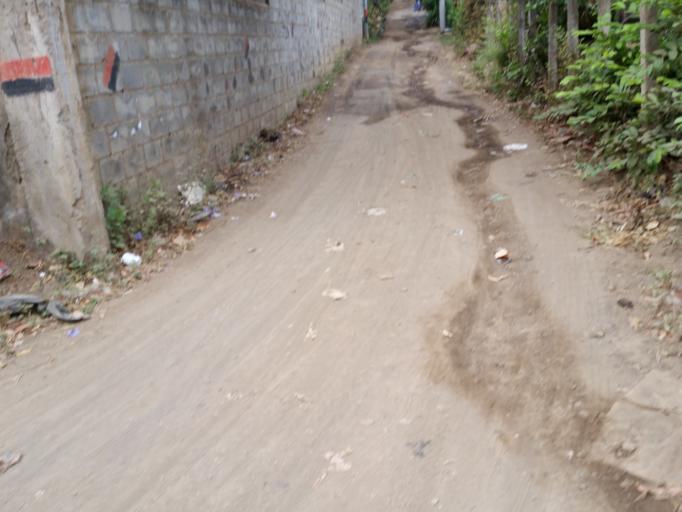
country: NI
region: Managua
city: Managua
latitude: 12.0976
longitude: -86.2508
